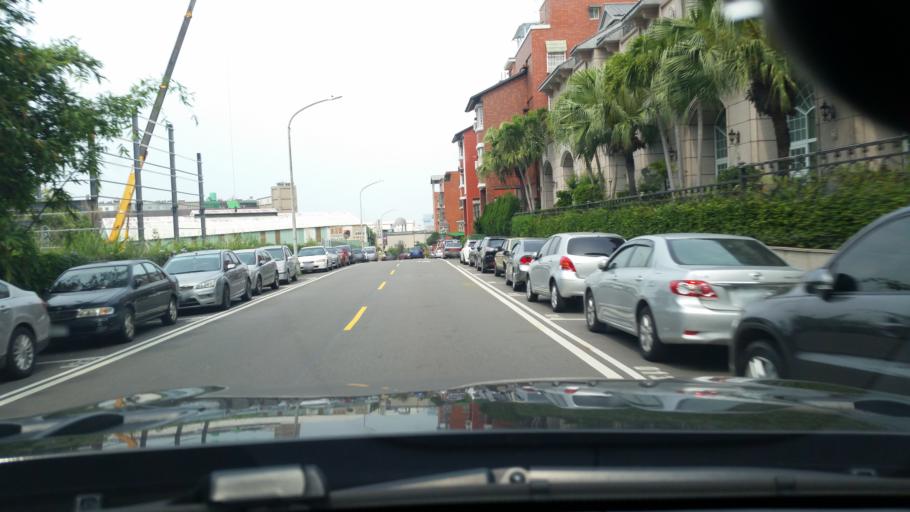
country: TW
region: Taiwan
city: Taoyuan City
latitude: 25.0615
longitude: 121.2955
